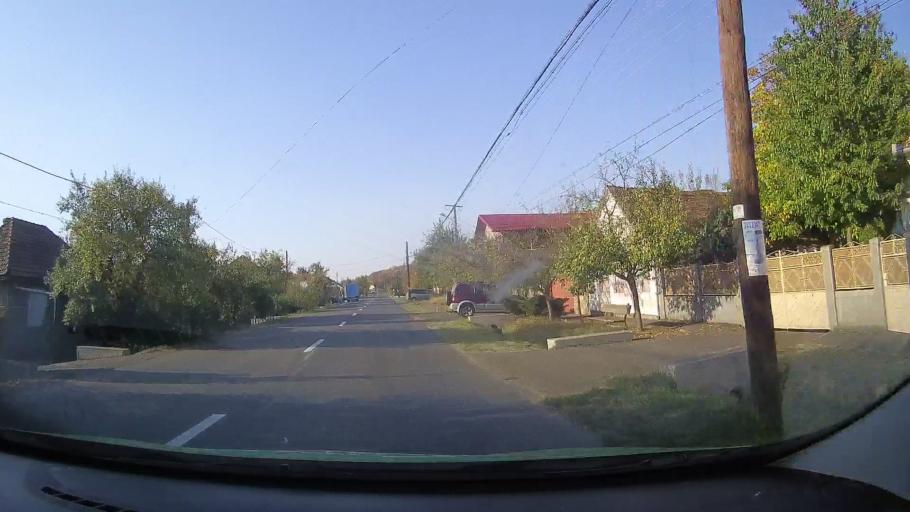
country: RO
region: Arad
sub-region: Comuna Ghioroc
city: Ghioroc
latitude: 46.1416
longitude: 21.6021
